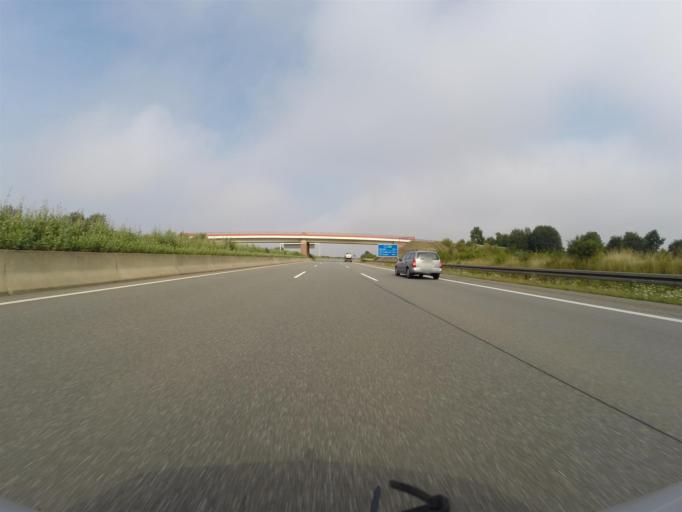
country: DE
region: Thuringia
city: Horselgau
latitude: 50.9067
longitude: 10.6012
